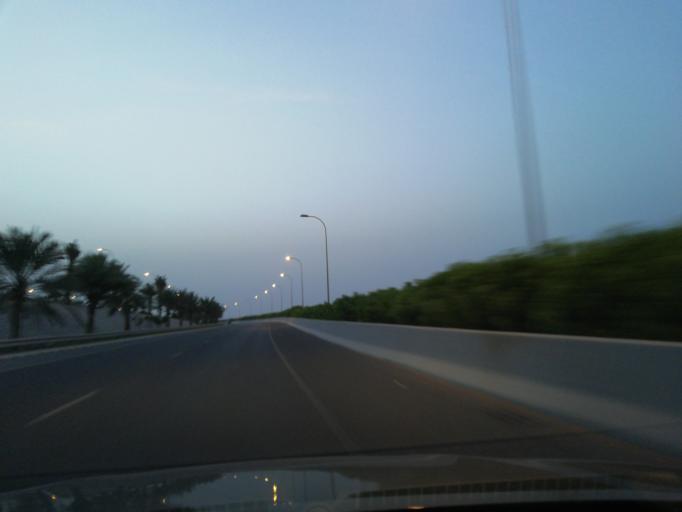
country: OM
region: Muhafazat Masqat
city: Bawshar
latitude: 23.5948
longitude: 58.3368
